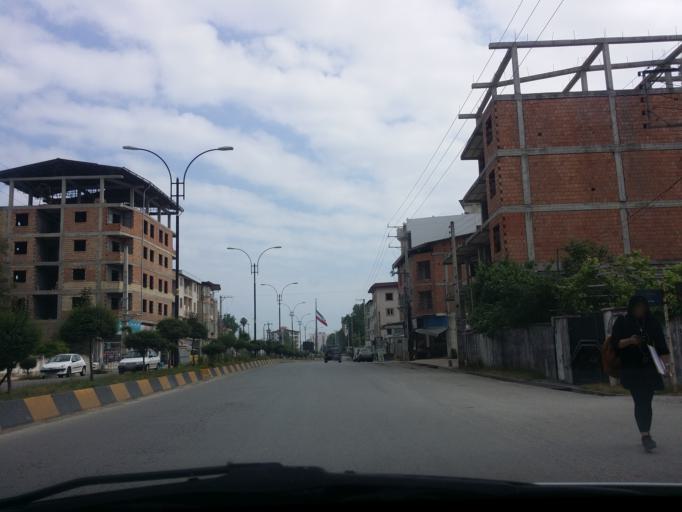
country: IR
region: Mazandaran
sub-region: Nowshahr
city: Nowshahr
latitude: 36.6362
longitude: 51.4884
